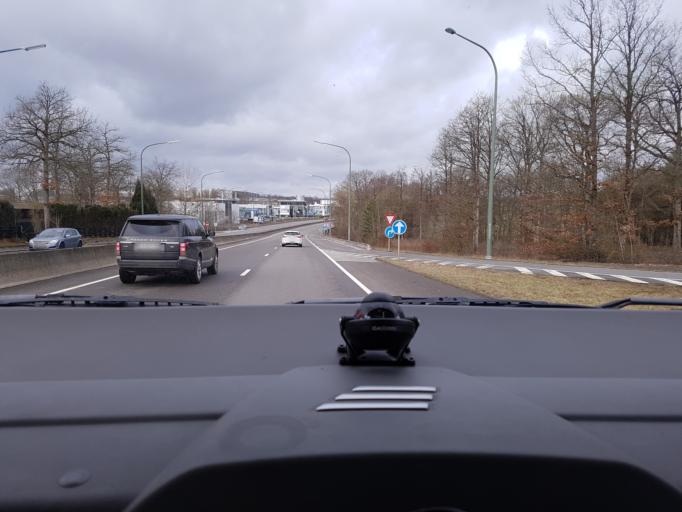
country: BE
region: Wallonia
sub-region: Province du Luxembourg
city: Marche-en-Famenne
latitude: 50.2381
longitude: 5.2961
